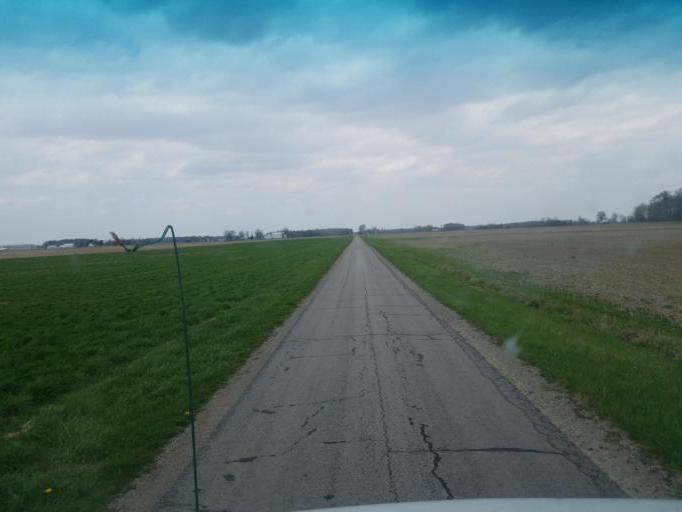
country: US
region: Ohio
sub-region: Crawford County
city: Bucyrus
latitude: 40.9532
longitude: -82.9972
